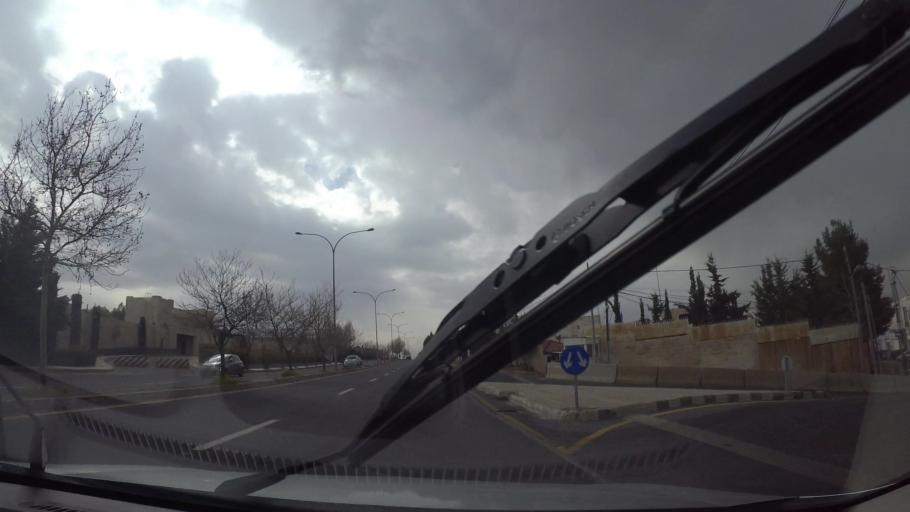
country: JO
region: Amman
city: Wadi as Sir
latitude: 31.9822
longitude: 35.8216
